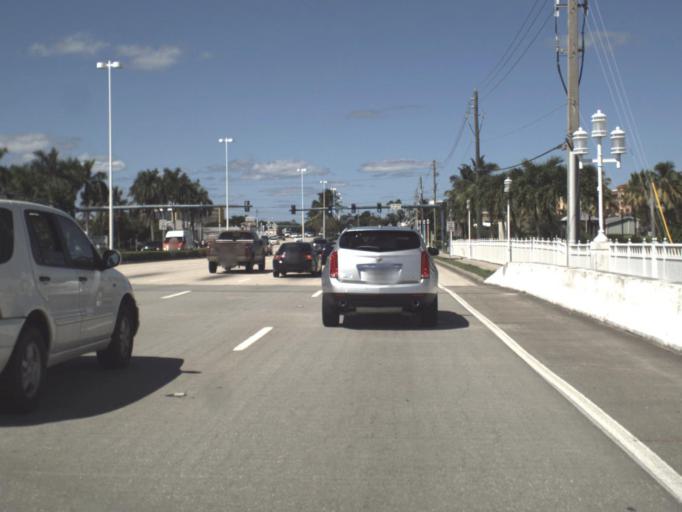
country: US
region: Florida
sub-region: Collier County
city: Naples
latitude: 26.1405
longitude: -81.7868
